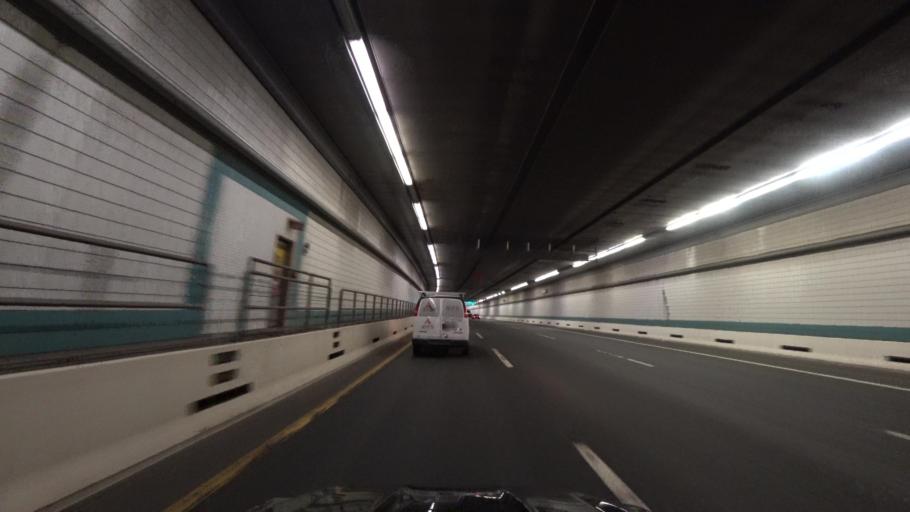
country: US
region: Massachusetts
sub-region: Suffolk County
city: Chelsea
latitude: 42.3630
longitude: -71.0268
